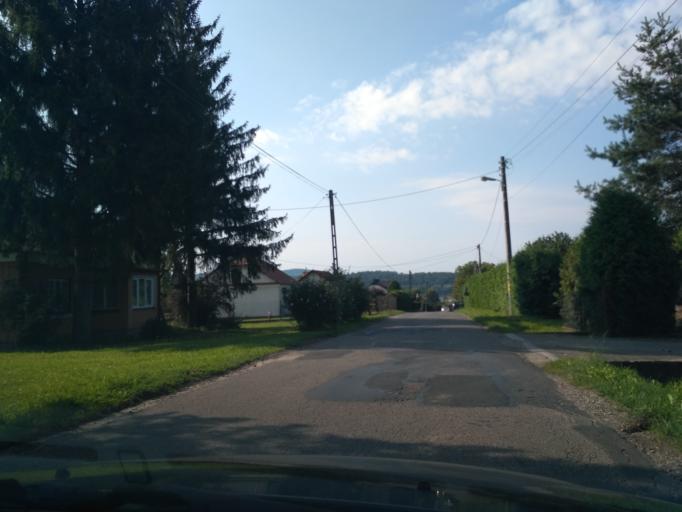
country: PL
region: Subcarpathian Voivodeship
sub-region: Powiat strzyzowski
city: Strzyzow
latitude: 49.8798
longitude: 21.7557
